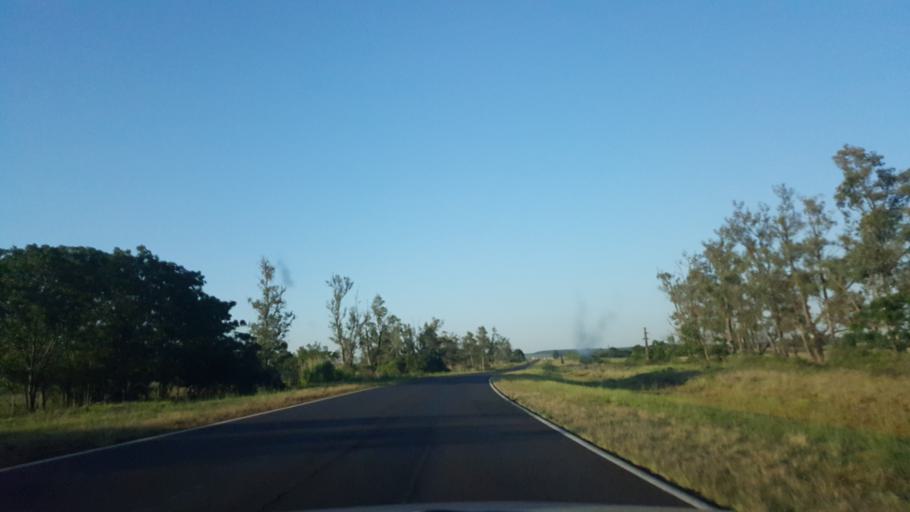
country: AR
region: Corrientes
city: Santo Tome
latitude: -28.4875
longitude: -56.1155
